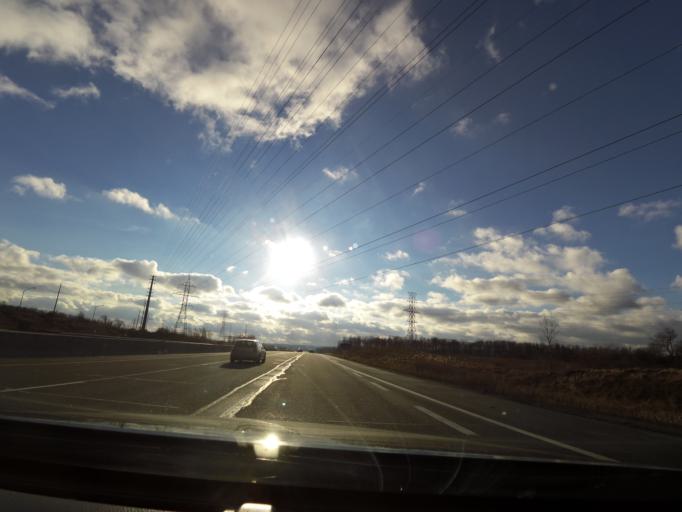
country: CA
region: Ontario
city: Burlington
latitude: 43.4274
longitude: -79.8067
